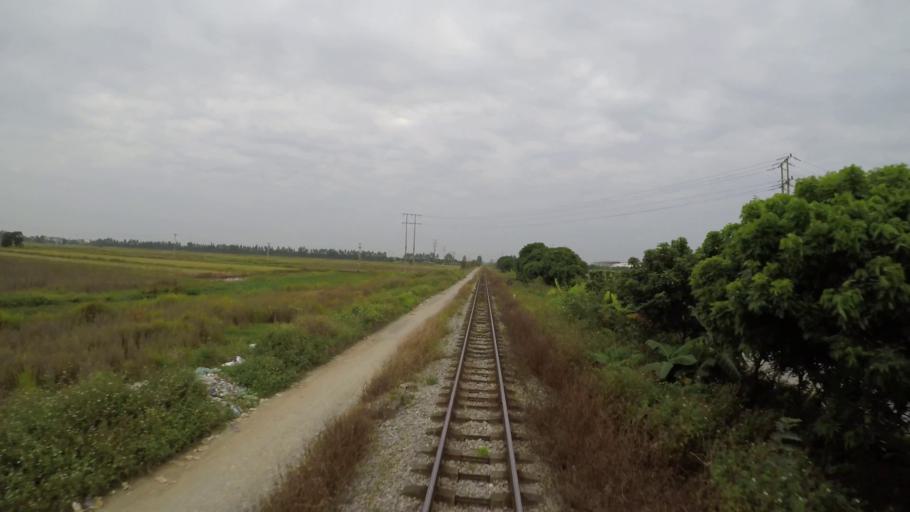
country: VN
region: Hai Duong
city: Lai Cach
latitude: 20.9480
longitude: 106.2561
